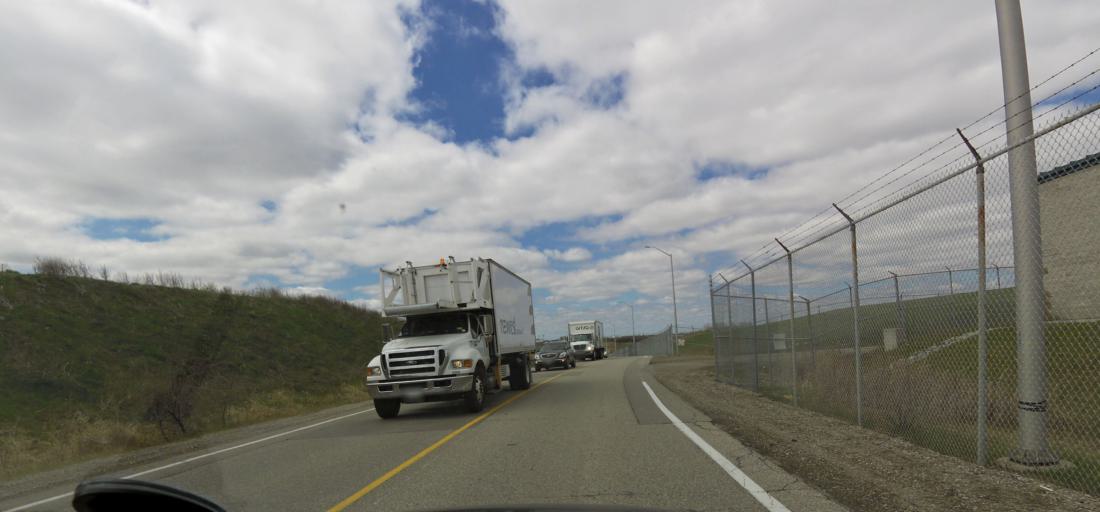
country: CA
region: Ontario
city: Etobicoke
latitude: 43.6690
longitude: -79.6355
